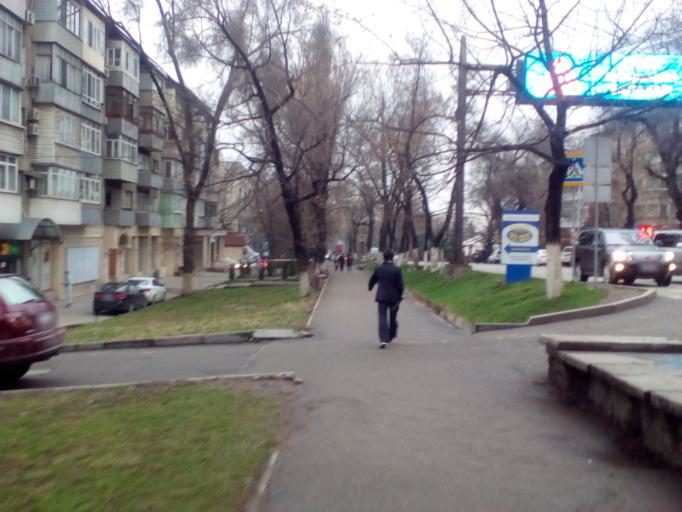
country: KZ
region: Almaty Qalasy
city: Almaty
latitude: 43.2227
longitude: 76.9627
